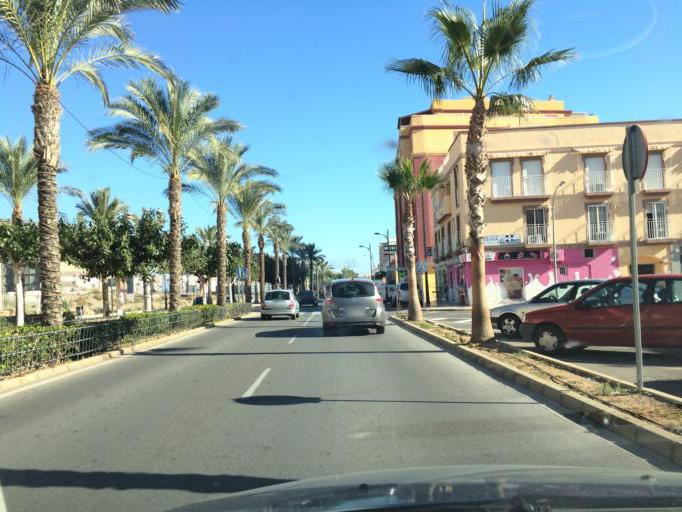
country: ES
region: Andalusia
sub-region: Provincia de Almeria
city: Aguadulce
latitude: 36.8100
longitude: -2.5904
